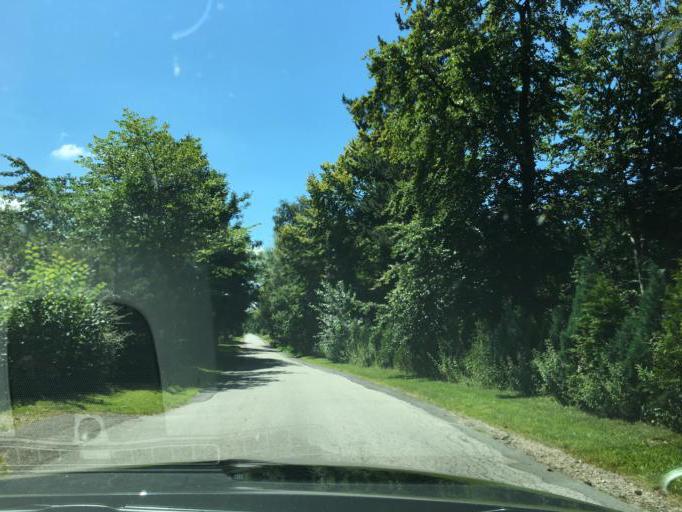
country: DK
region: Capital Region
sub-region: Gribskov Kommune
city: Helsinge
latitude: 56.0906
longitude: 12.1703
